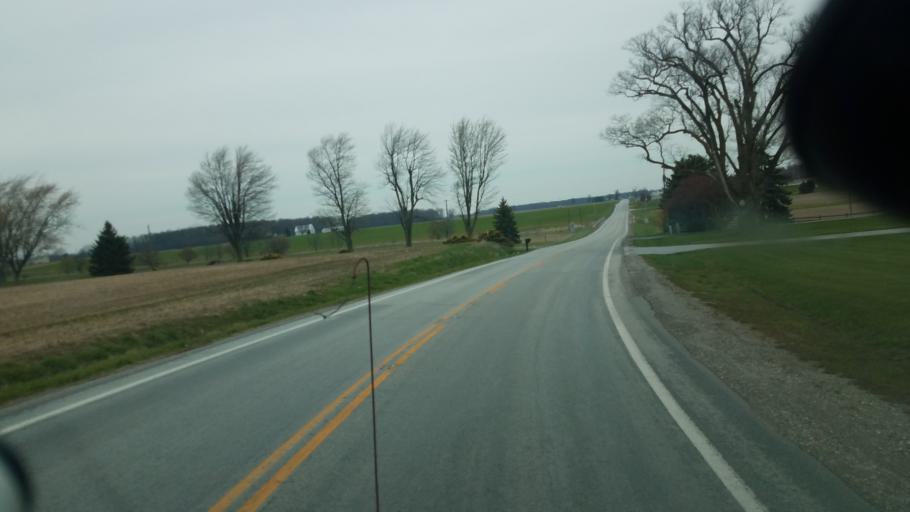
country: US
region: Ohio
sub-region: Hardin County
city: Forest
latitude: 40.8697
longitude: -83.5247
